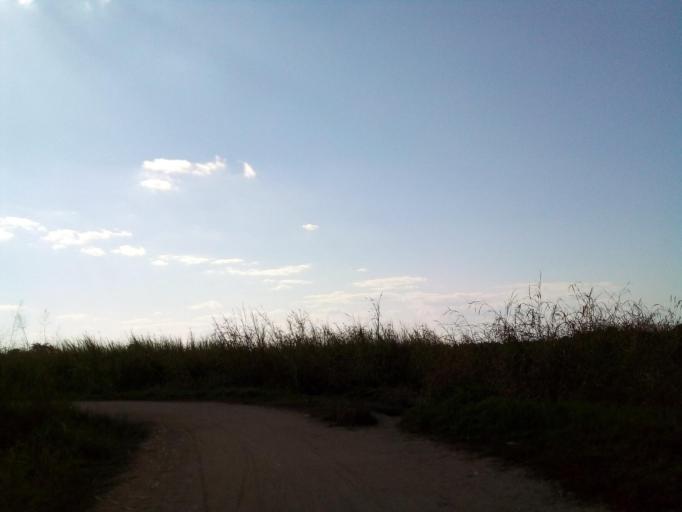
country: MZ
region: Zambezia
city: Quelimane
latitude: -17.5523
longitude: 36.6979
